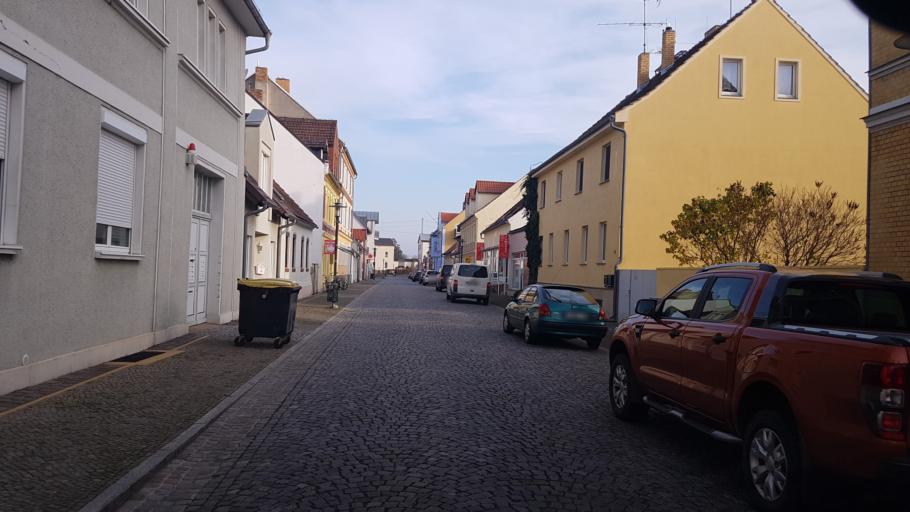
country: DE
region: Brandenburg
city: Falkenberg
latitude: 51.5859
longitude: 13.2423
